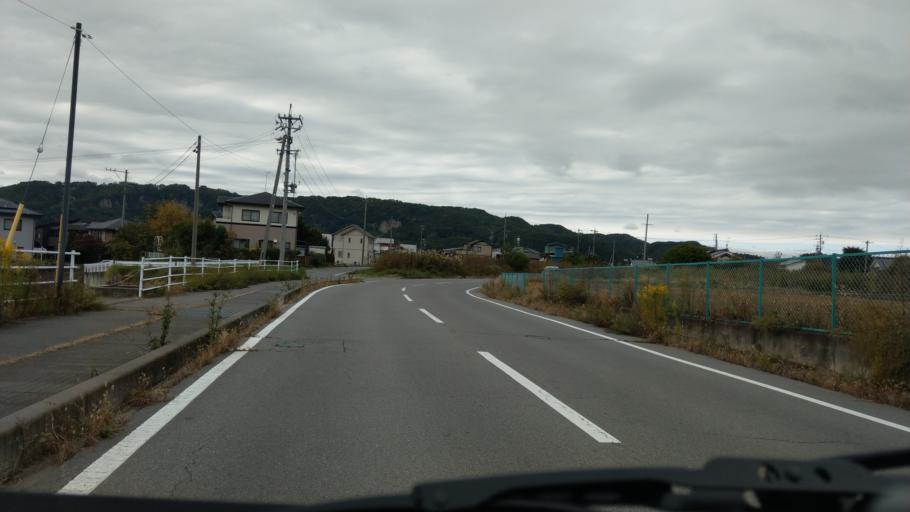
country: JP
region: Nagano
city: Komoro
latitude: 36.3120
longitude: 138.4325
